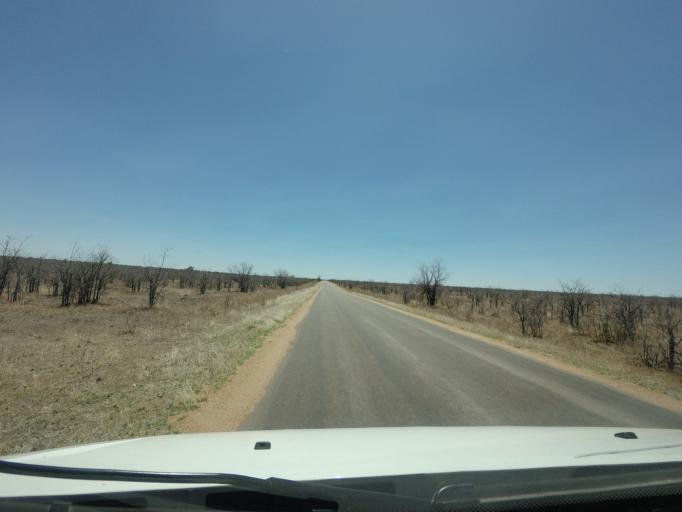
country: ZA
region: Limpopo
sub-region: Mopani District Municipality
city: Phalaborwa
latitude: -23.5783
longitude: 31.4507
